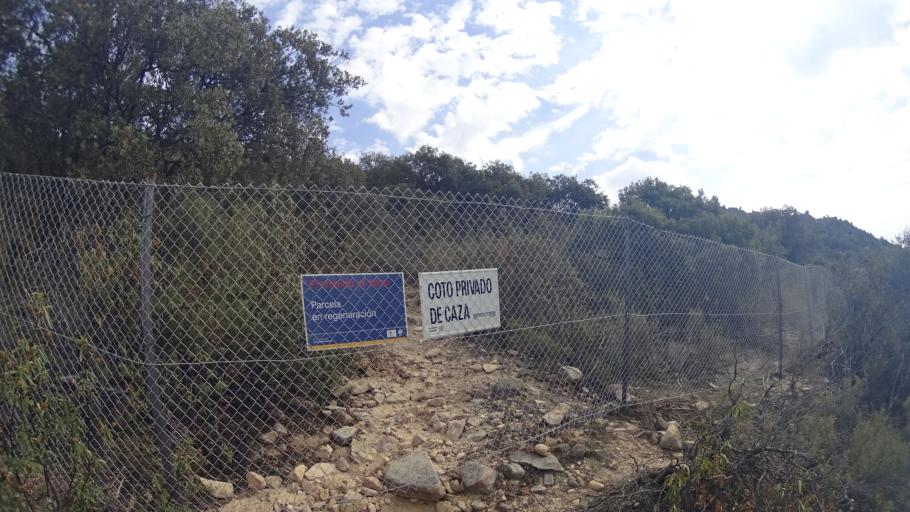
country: ES
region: Madrid
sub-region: Provincia de Madrid
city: Hoyo de Manzanares
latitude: 40.6271
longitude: -3.9291
